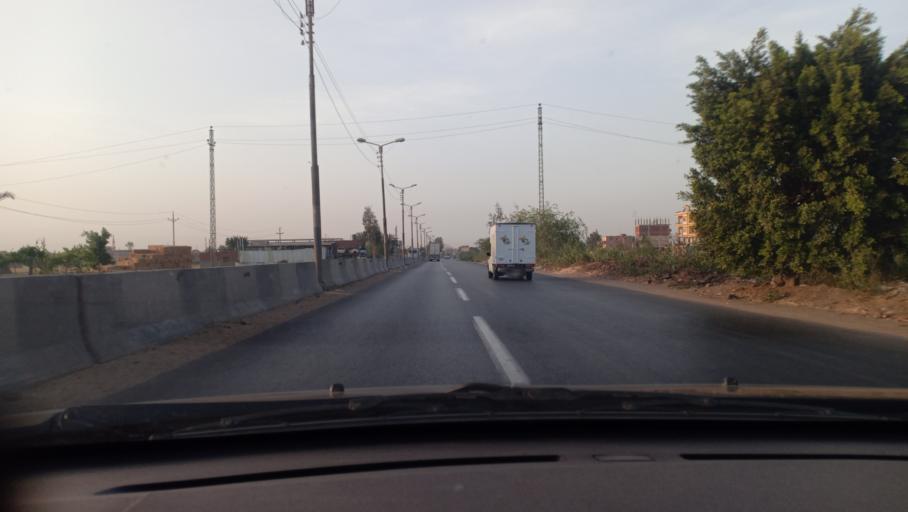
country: EG
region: Muhafazat al Gharbiyah
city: Zifta
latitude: 30.6164
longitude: 31.2771
